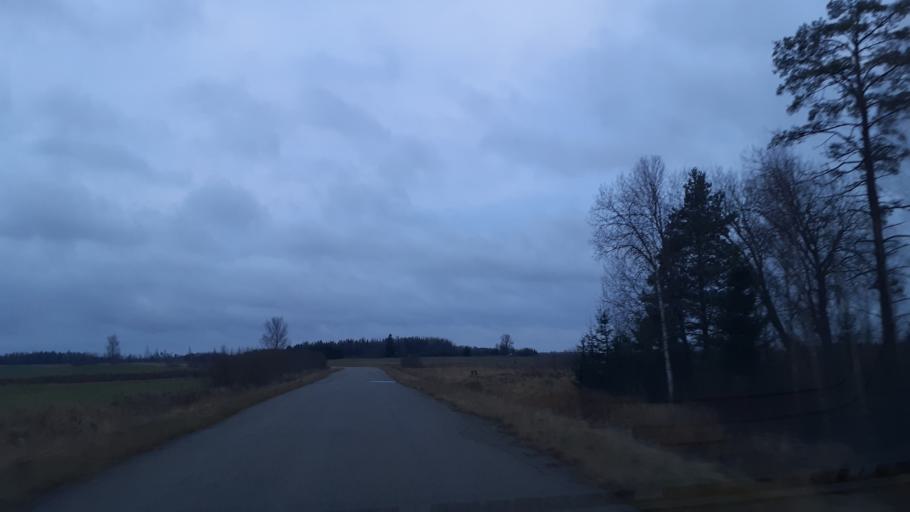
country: LV
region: Kuldigas Rajons
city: Kuldiga
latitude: 57.0316
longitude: 22.1576
